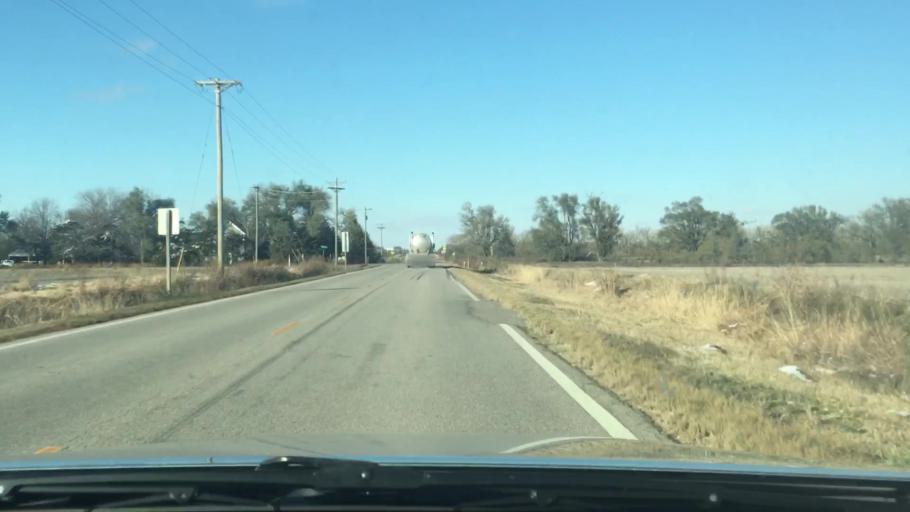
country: US
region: Kansas
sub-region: Rice County
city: Sterling
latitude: 38.1653
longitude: -98.2069
